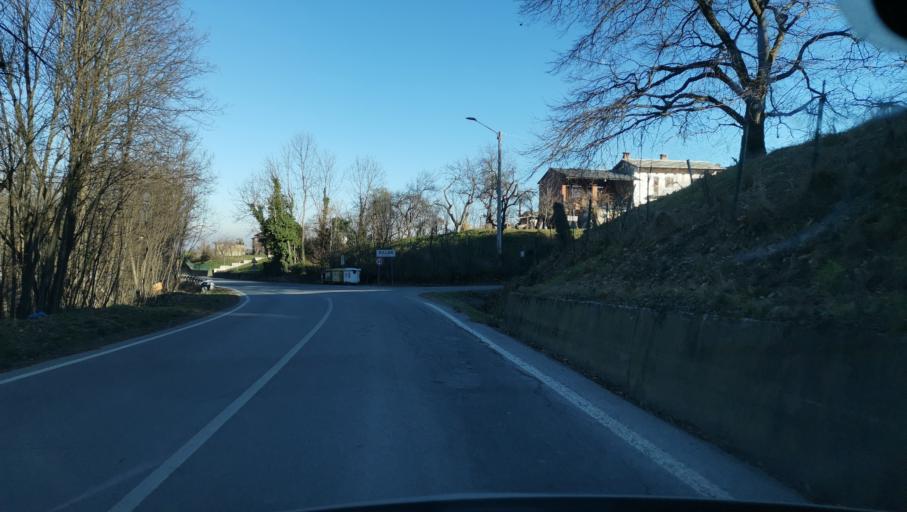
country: IT
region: Piedmont
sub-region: Provincia di Cuneo
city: Bagnolo Piemonte
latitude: 44.7530
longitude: 7.2860
